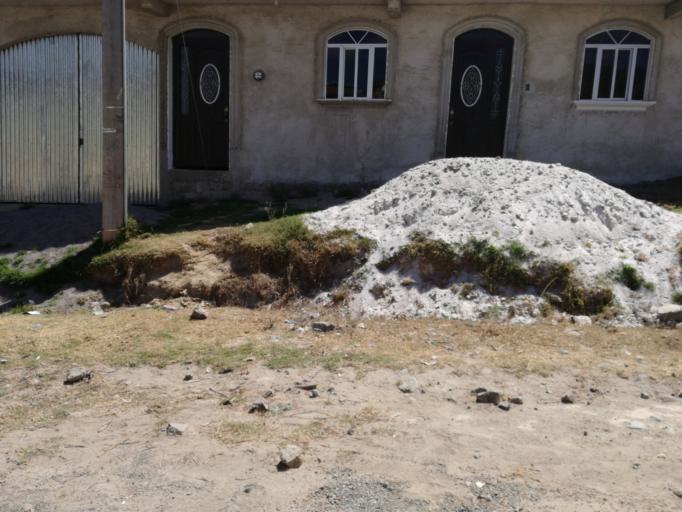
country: GT
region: Quetzaltenango
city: Almolonga
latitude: 14.7969
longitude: -91.5374
